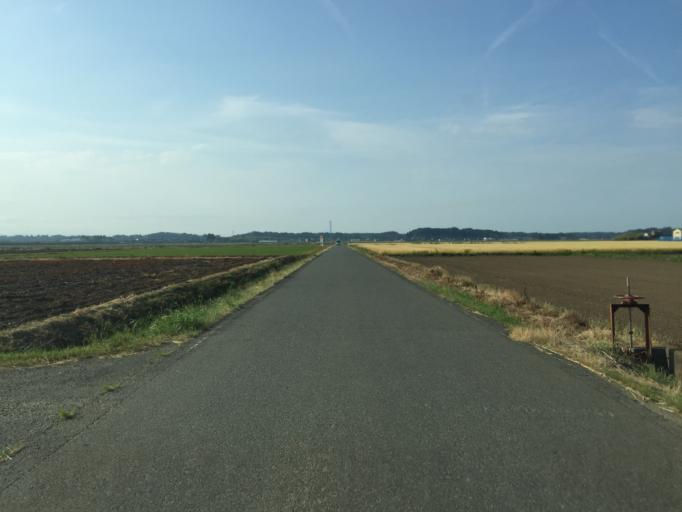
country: JP
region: Miyagi
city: Marumori
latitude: 37.7904
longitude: 140.9491
